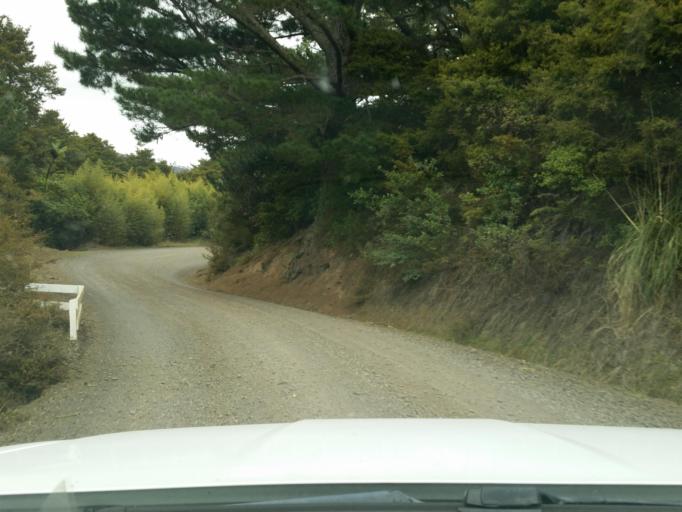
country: NZ
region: Northland
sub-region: Kaipara District
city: Dargaville
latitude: -35.7106
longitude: 173.6106
